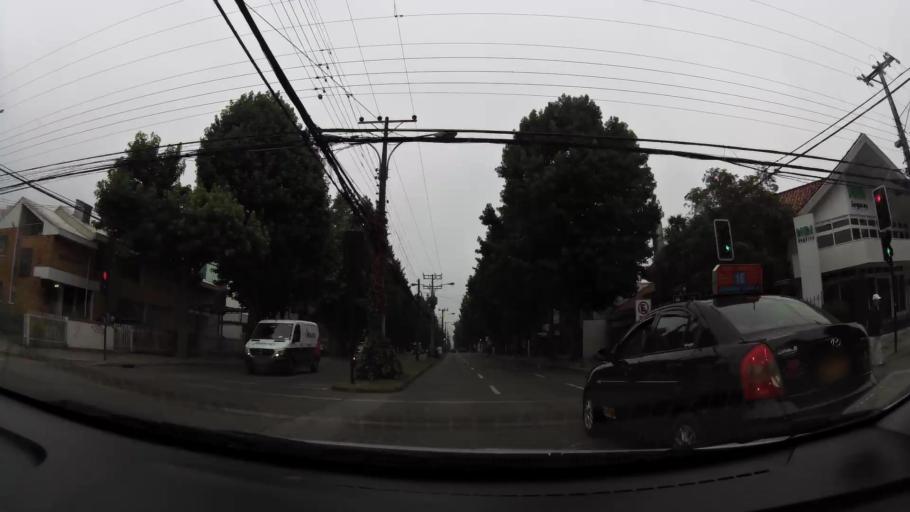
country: CL
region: Biobio
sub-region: Provincia de Concepcion
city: Concepcion
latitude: -36.8298
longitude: -73.0462
